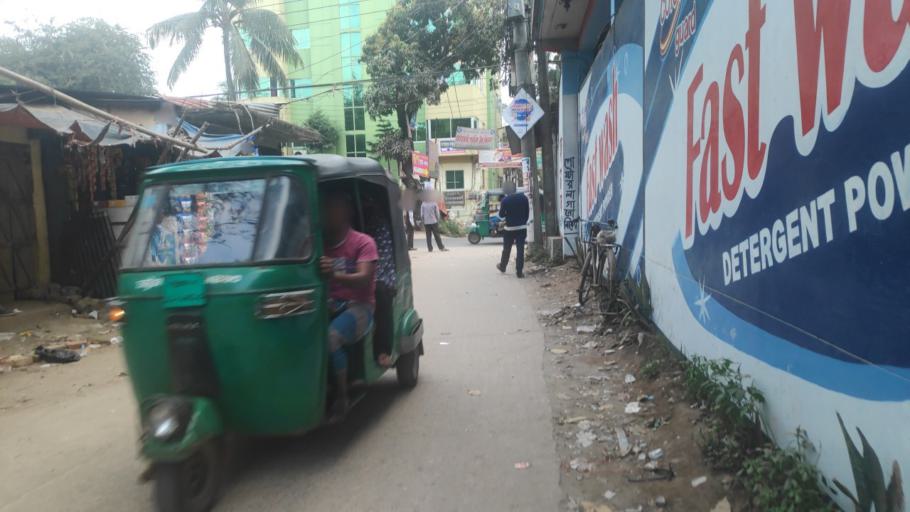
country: BD
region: Chittagong
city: Raojan
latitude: 22.5034
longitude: 91.8137
